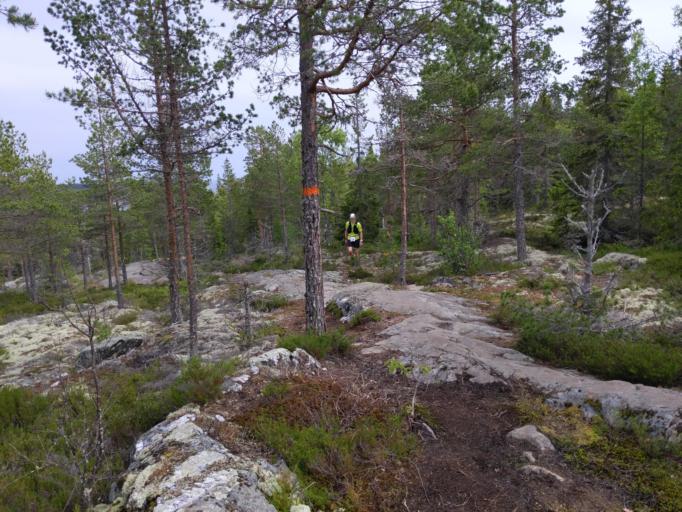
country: SE
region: Vaesternorrland
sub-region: OErnskoeldsviks Kommun
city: Ornskoldsvik
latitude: 63.1913
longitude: 18.7001
